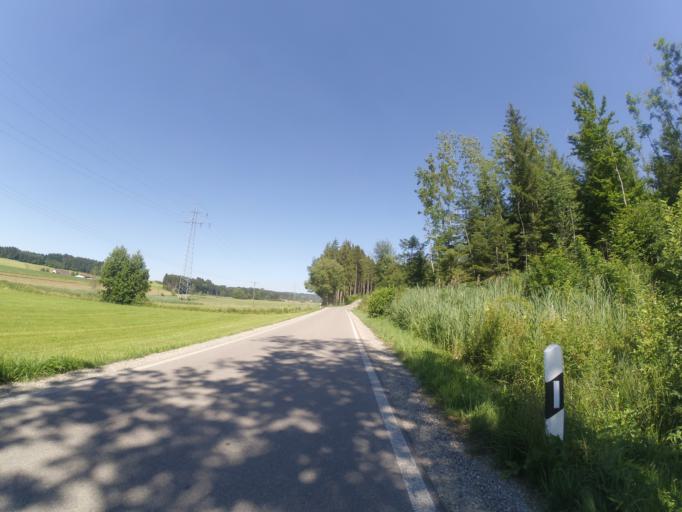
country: DE
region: Baden-Wuerttemberg
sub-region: Tuebingen Region
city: Bad Wurzach
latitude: 47.8534
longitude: 9.9408
